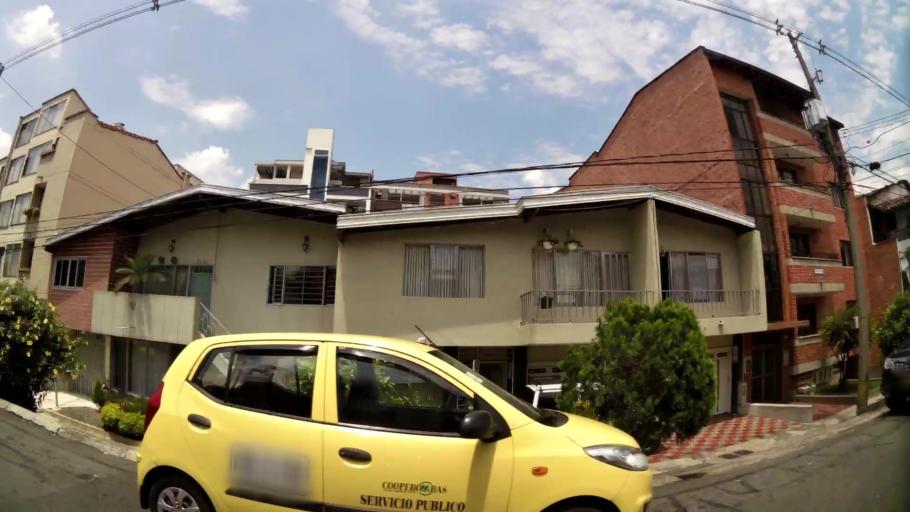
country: CO
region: Antioquia
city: Medellin
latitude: 6.2362
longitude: -75.5987
